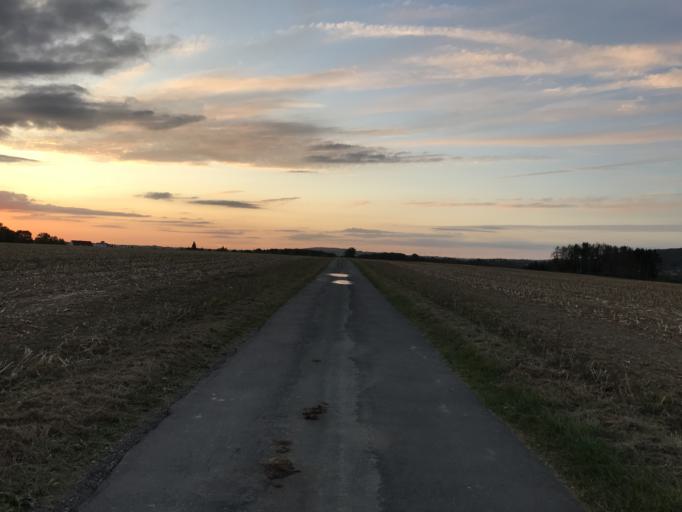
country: DE
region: North Rhine-Westphalia
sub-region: Regierungsbezirk Detmold
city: Lemgo
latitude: 52.0134
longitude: 8.9385
